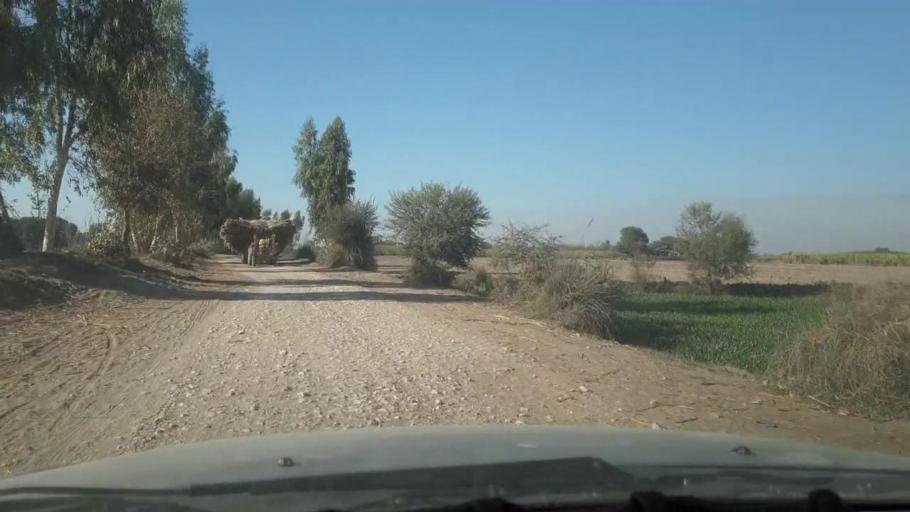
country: PK
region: Sindh
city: Pano Aqil
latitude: 27.9736
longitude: 69.1742
